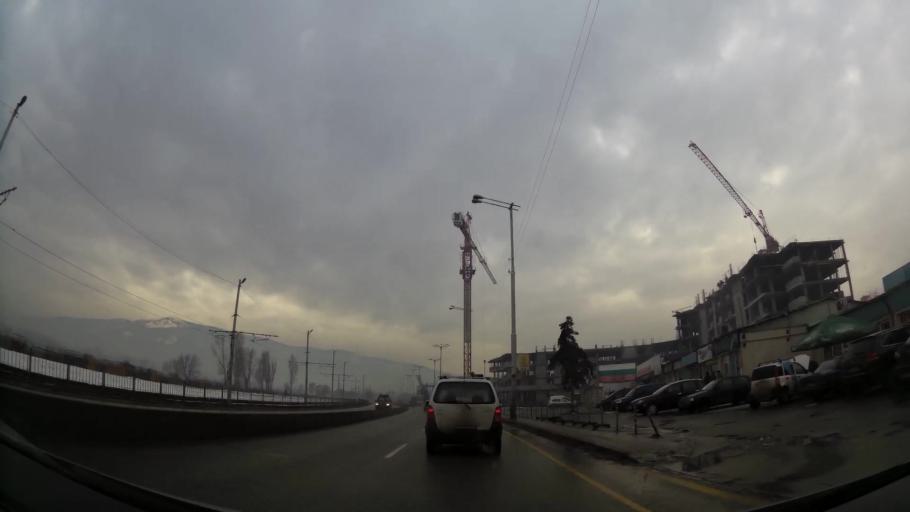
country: BG
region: Sofia-Capital
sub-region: Stolichna Obshtina
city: Sofia
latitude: 42.6907
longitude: 23.2780
